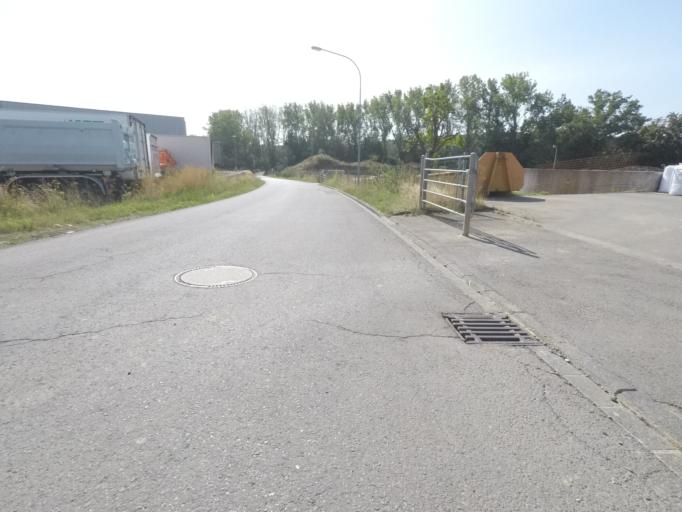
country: LU
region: Luxembourg
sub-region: Canton de Luxembourg
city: Olm
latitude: 49.6622
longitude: 6.0133
